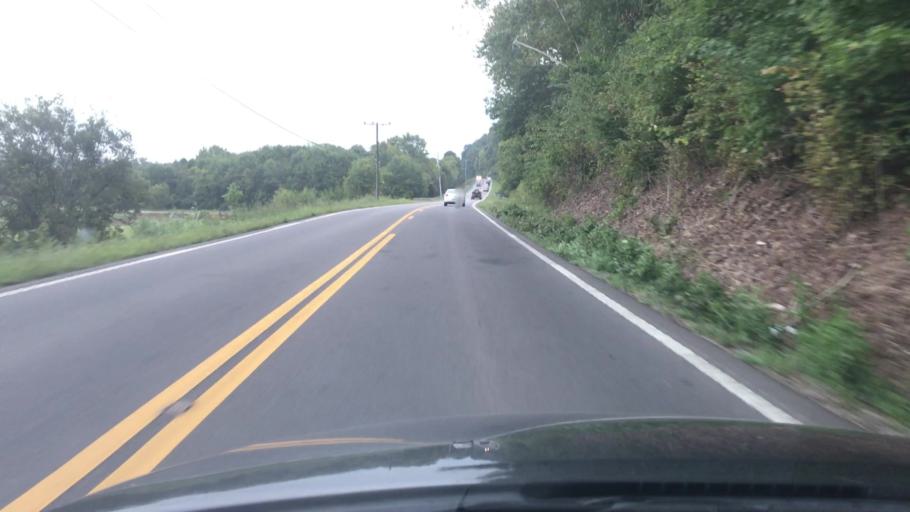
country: US
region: Tennessee
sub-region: Cheatham County
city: Ashland City
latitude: 36.2765
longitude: -87.0925
